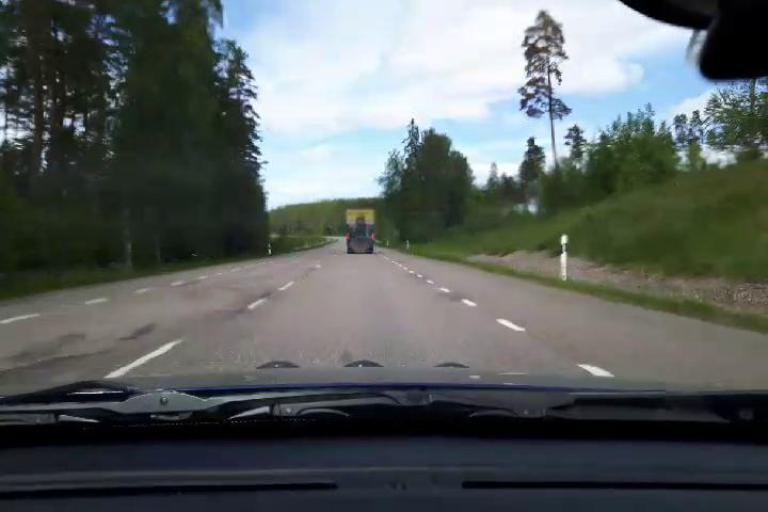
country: SE
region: Uppsala
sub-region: Osthammars Kommun
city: Bjorklinge
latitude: 60.0969
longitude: 17.5538
